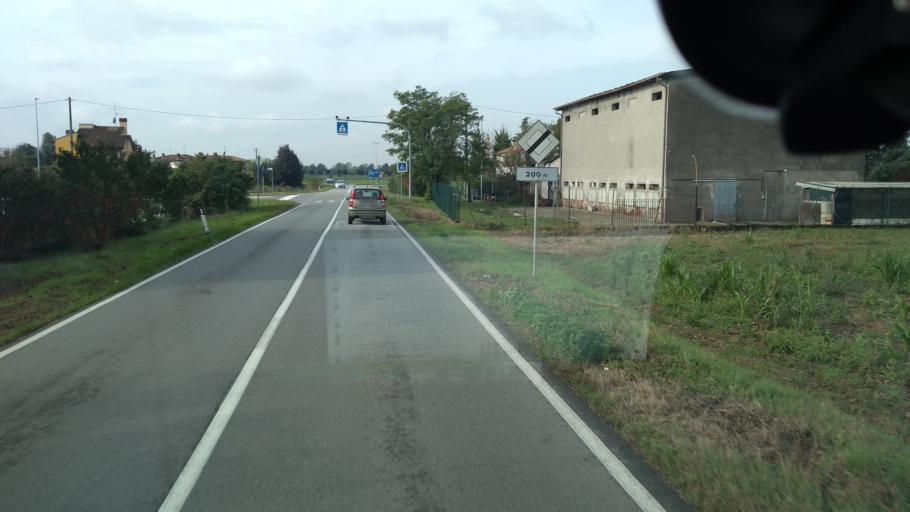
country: IT
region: Lombardy
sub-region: Provincia di Bergamo
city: Brignano Gera d'Adda
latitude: 45.5510
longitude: 9.6470
